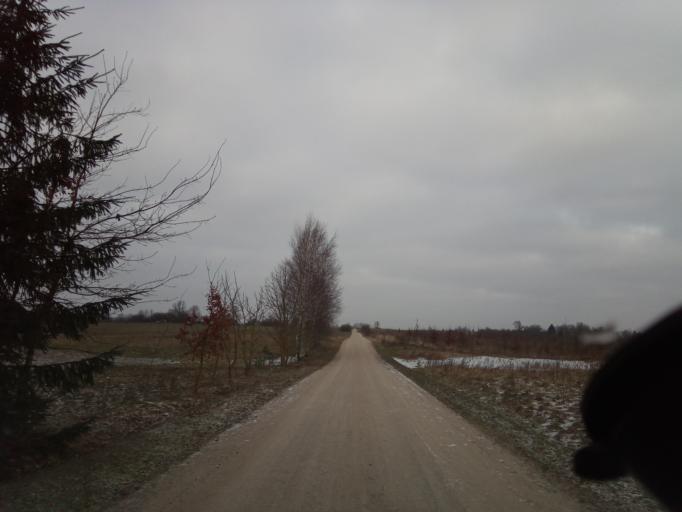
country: LT
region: Alytaus apskritis
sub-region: Alytaus rajonas
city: Daugai
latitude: 54.3738
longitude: 24.4447
